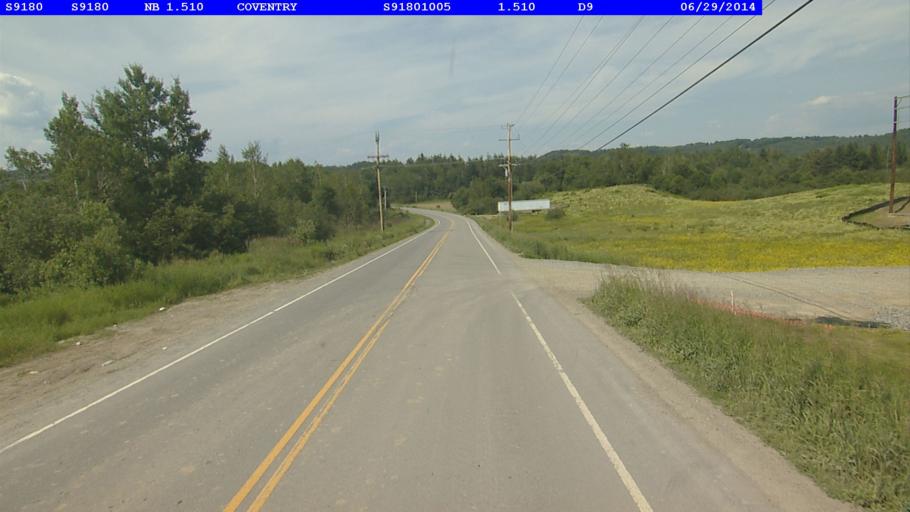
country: US
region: Vermont
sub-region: Orleans County
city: Newport
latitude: 44.9100
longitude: -72.2201
